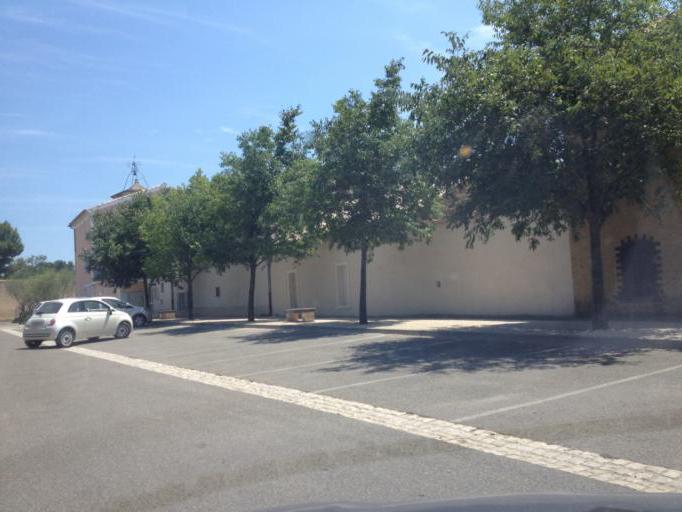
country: FR
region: Provence-Alpes-Cote d'Azur
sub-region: Departement du Vaucluse
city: Uchaux
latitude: 44.2099
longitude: 4.7998
